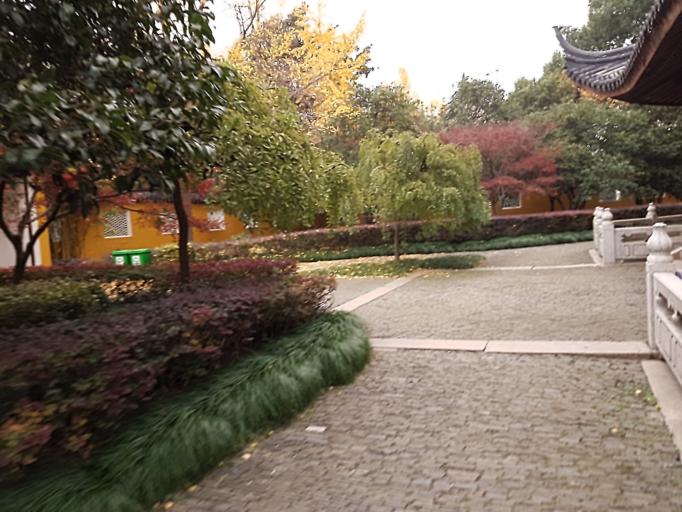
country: CN
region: Jiangsu Sheng
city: Pingjianglu
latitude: 31.3247
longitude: 120.6153
